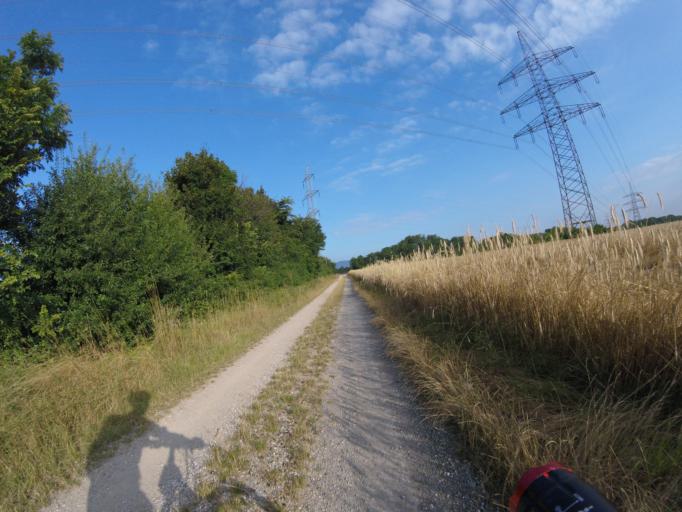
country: AT
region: Lower Austria
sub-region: Politischer Bezirk Baden
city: Trumau
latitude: 47.9946
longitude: 16.3743
